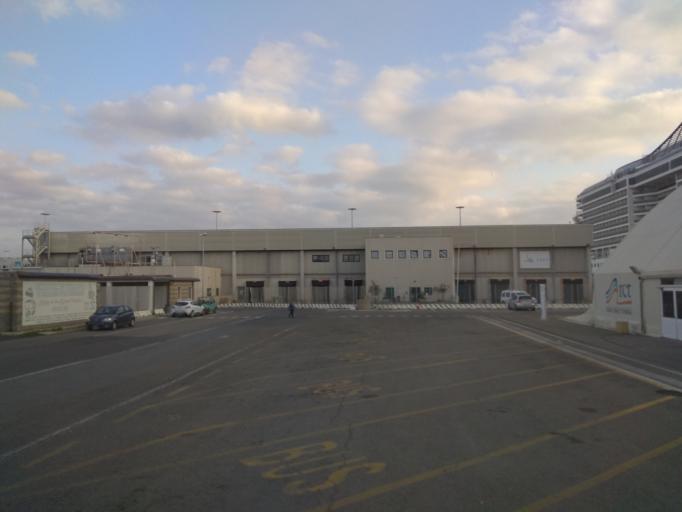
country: IT
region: Latium
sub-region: Citta metropolitana di Roma Capitale
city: Civitavecchia
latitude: 42.1036
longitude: 11.7744
